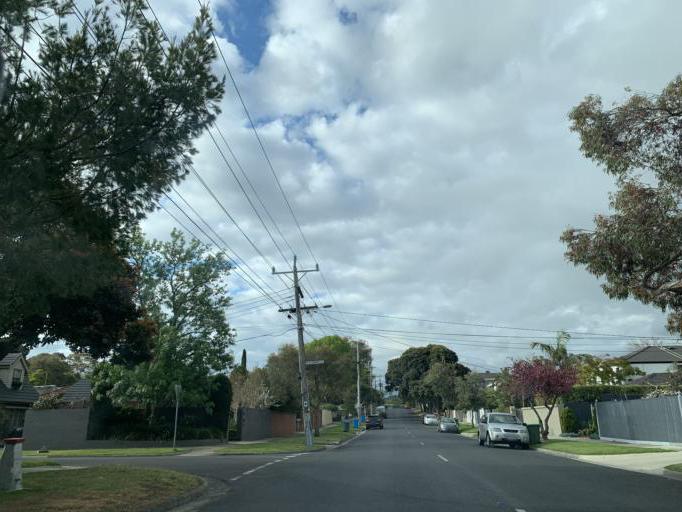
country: AU
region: Victoria
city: Beaumaris
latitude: -37.9806
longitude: 145.0388
